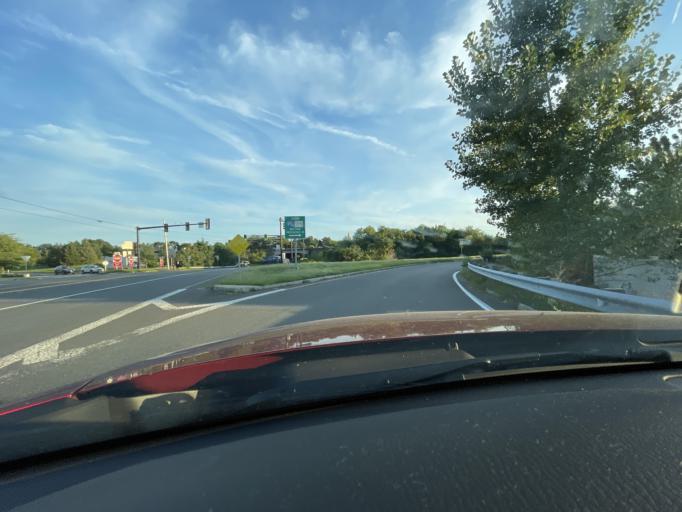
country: US
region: Massachusetts
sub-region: Essex County
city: Lynnfield
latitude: 42.5143
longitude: -71.0416
